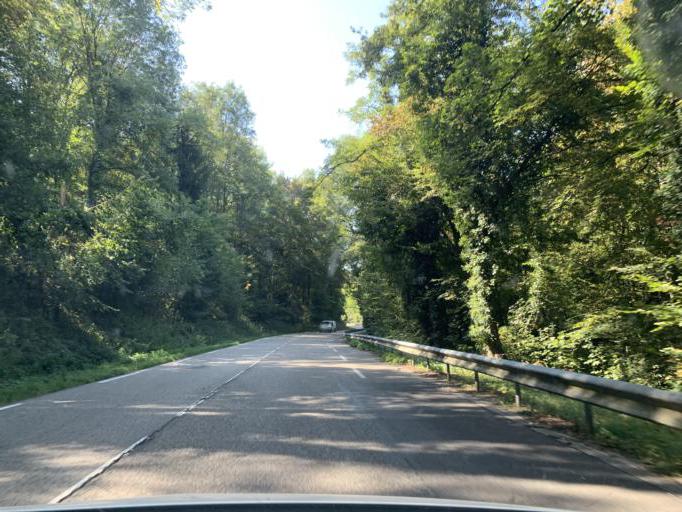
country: FR
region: Rhone-Alpes
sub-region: Departement de l'Ain
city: Belley
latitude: 45.7357
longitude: 5.6715
